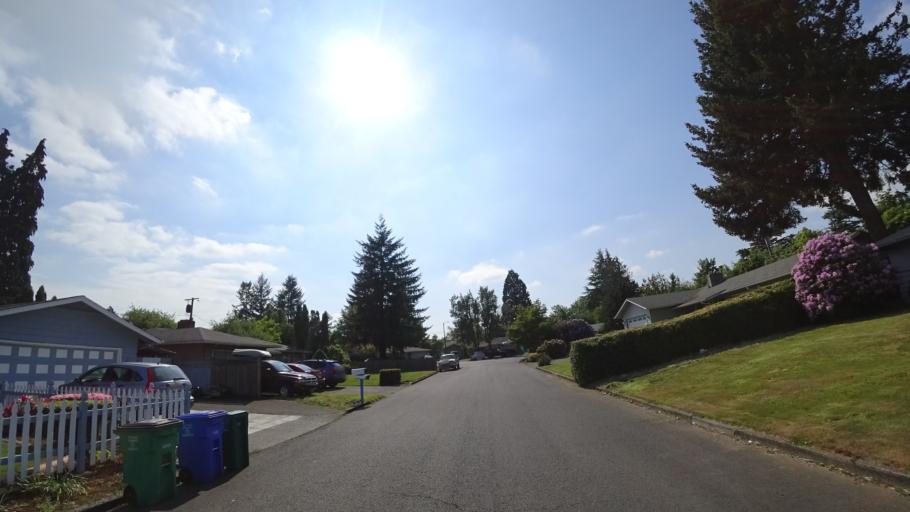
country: US
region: Oregon
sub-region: Multnomah County
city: Fairview
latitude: 45.5171
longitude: -122.4946
